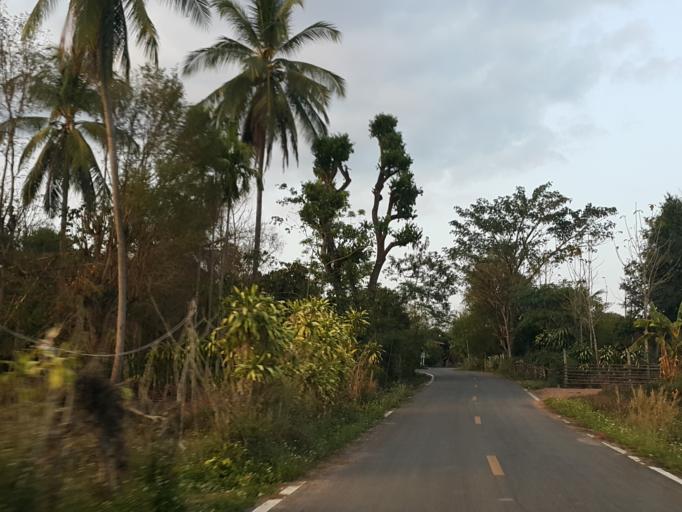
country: TH
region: Lampang
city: Mueang Pan
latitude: 18.7864
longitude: 99.4954
